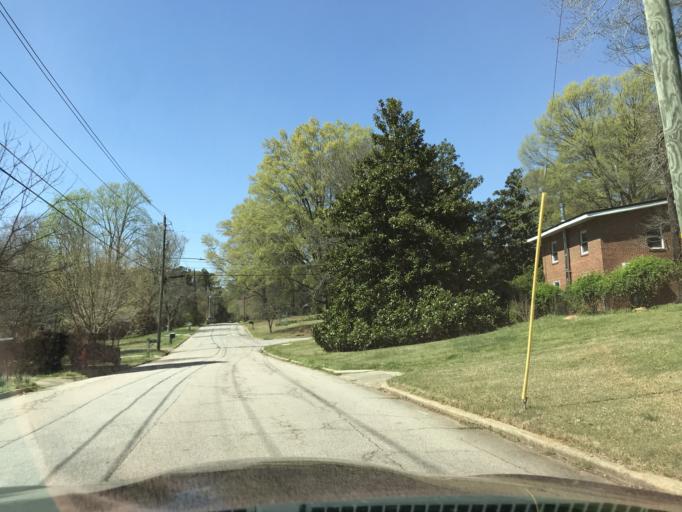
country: US
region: North Carolina
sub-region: Wake County
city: West Raleigh
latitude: 35.7732
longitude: -78.7083
